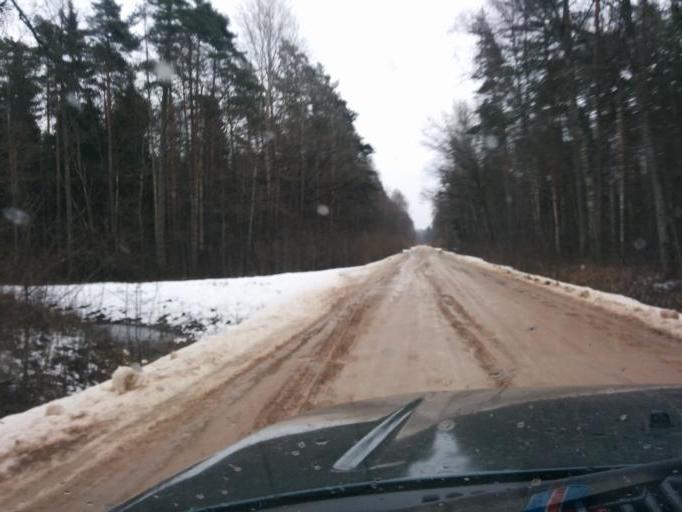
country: LV
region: Ozolnieku
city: Ozolnieki
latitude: 56.6861
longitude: 23.7675
